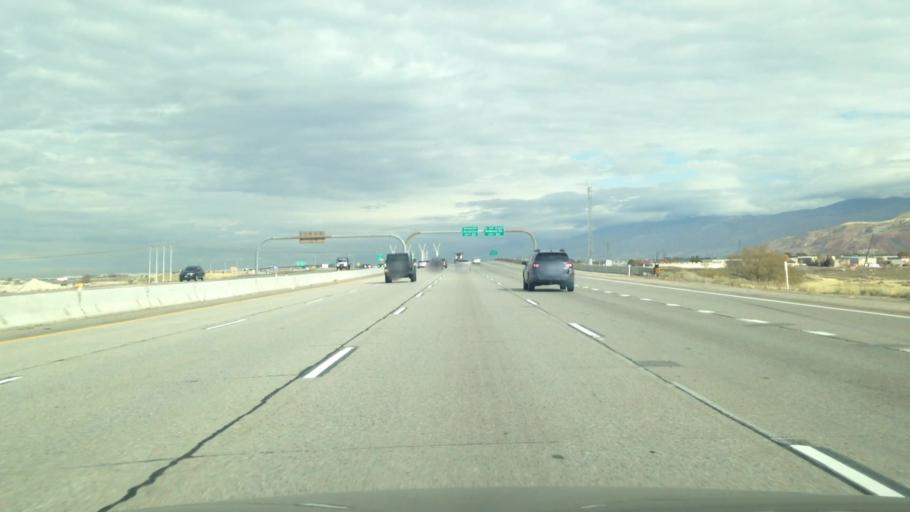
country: US
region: Utah
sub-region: Salt Lake County
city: Salt Lake City
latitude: 40.7494
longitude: -111.9486
